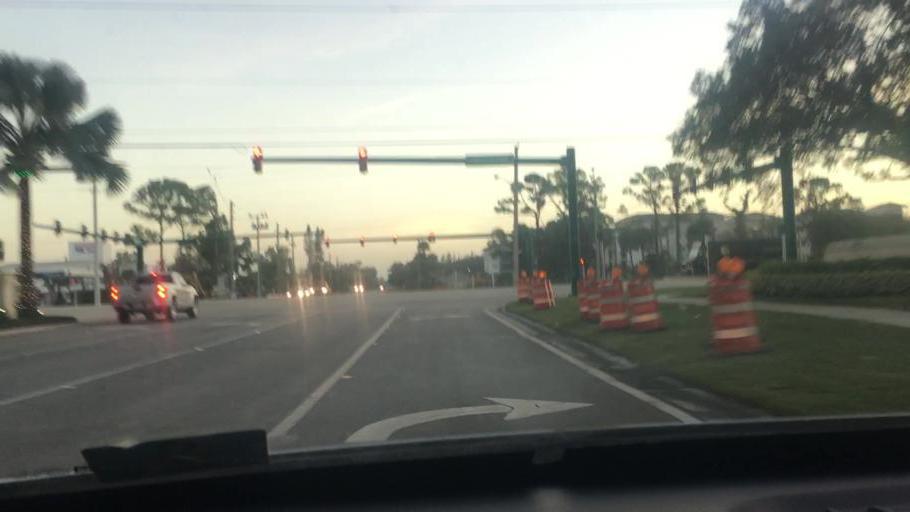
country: US
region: Florida
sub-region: Palm Beach County
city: Plantation Mobile Home Park
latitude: 26.7088
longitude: -80.1580
